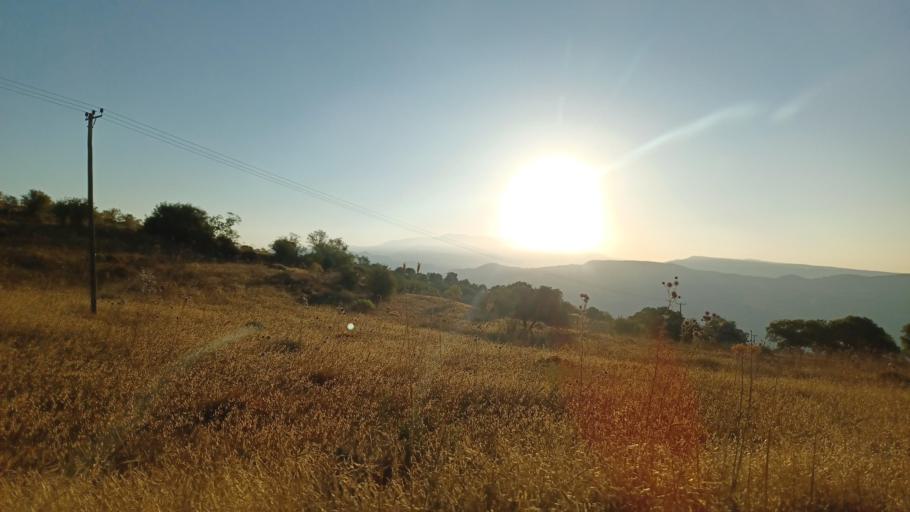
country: CY
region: Pafos
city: Mesogi
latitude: 34.8605
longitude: 32.6189
